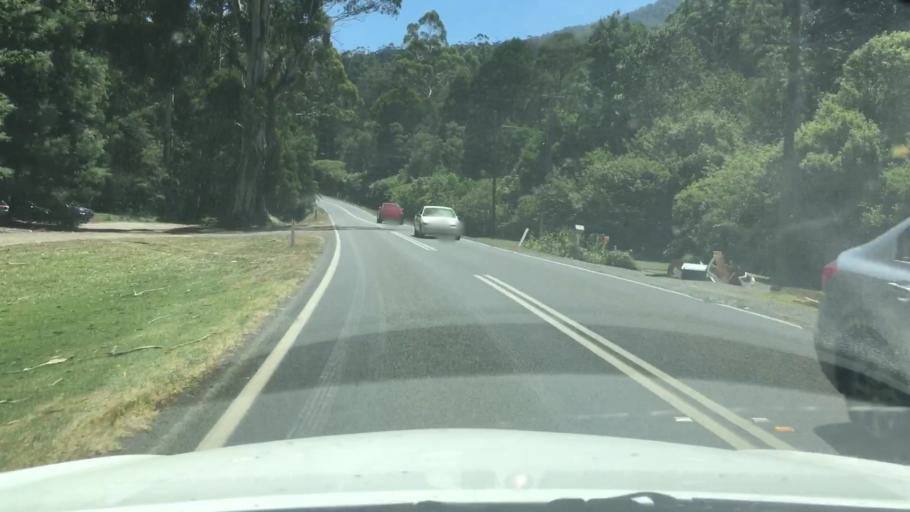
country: AU
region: Victoria
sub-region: Yarra Ranges
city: Millgrove
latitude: -37.7478
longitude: 145.7170
